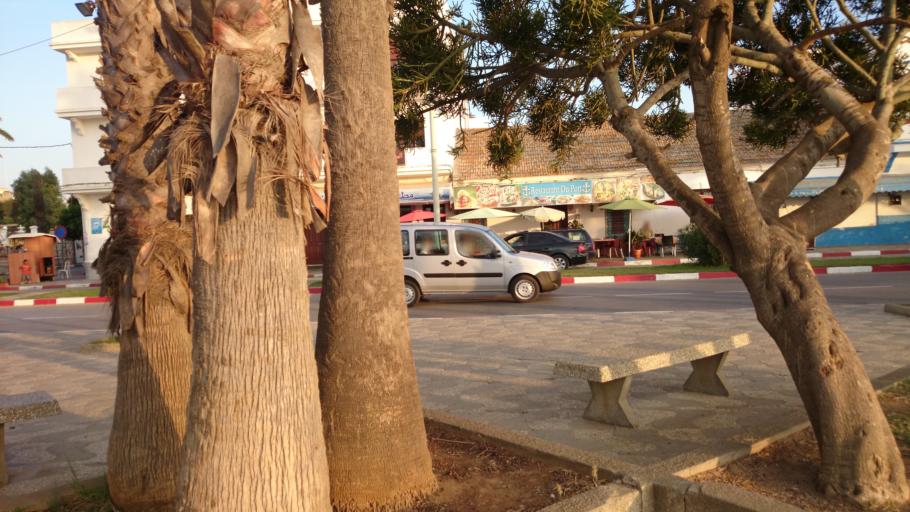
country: MA
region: Tanger-Tetouan
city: Asilah
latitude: 35.4680
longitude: -6.0350
